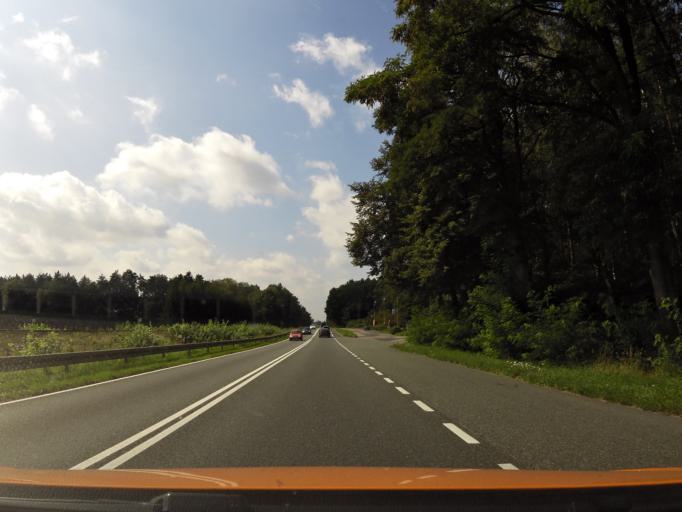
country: PL
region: West Pomeranian Voivodeship
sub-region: Powiat goleniowski
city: Nowogard
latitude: 53.6995
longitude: 15.1652
